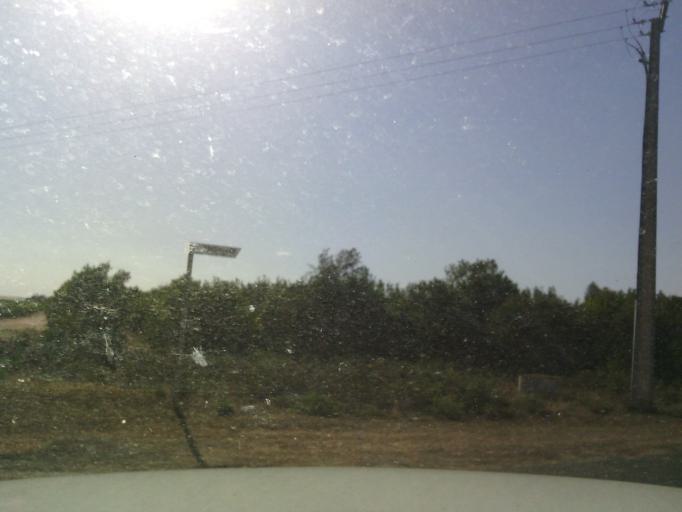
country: AU
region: South Australia
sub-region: Berri and Barmera
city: Berri
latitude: -34.2810
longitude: 140.5660
